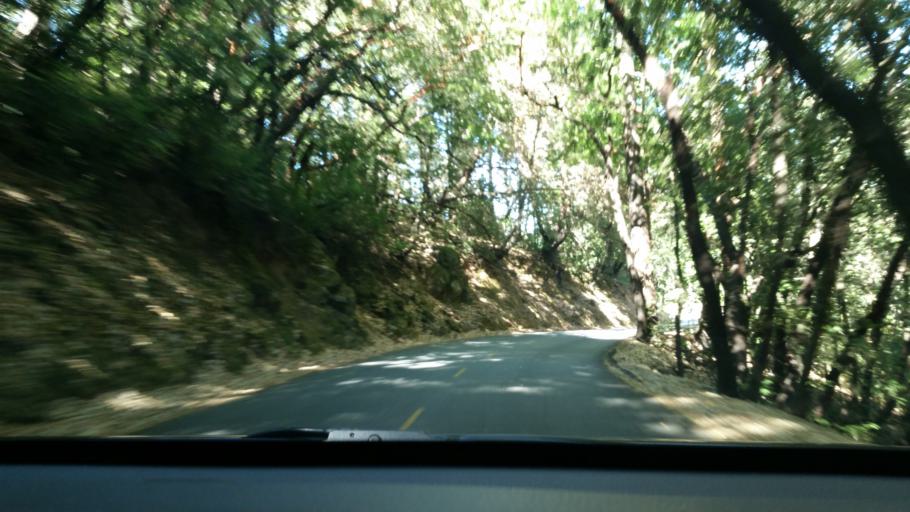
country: US
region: California
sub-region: San Mateo County
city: Woodside
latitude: 37.4275
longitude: -122.3049
